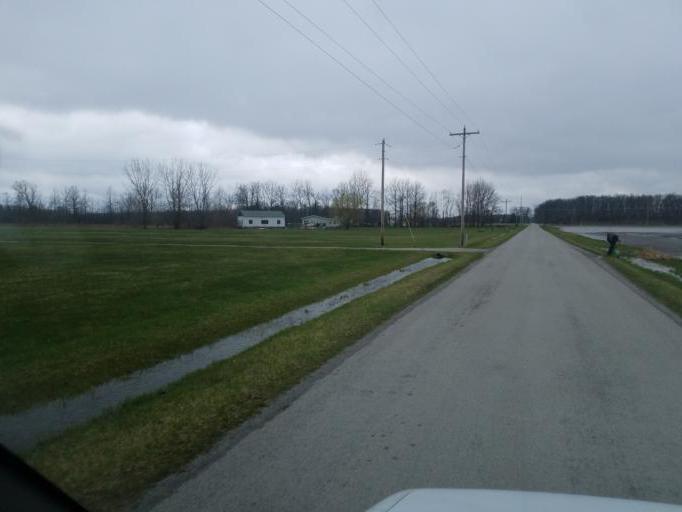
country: US
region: Ohio
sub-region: Wyandot County
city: Upper Sandusky
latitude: 40.6872
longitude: -83.3196
